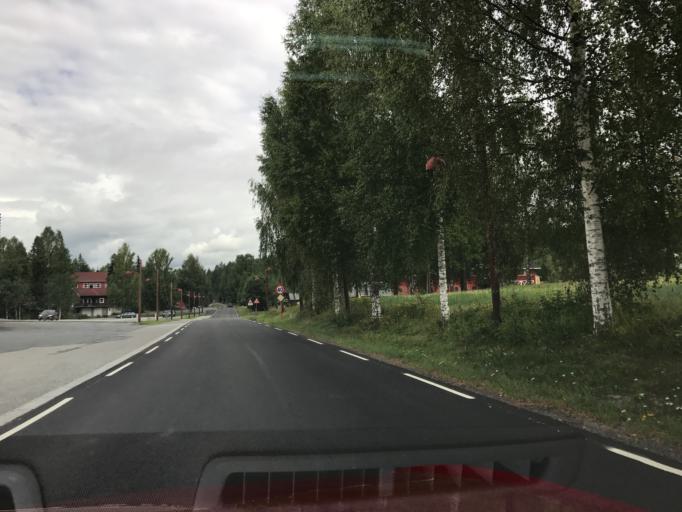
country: NO
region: Buskerud
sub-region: Flesberg
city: Lampeland
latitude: 59.8351
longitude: 9.5792
